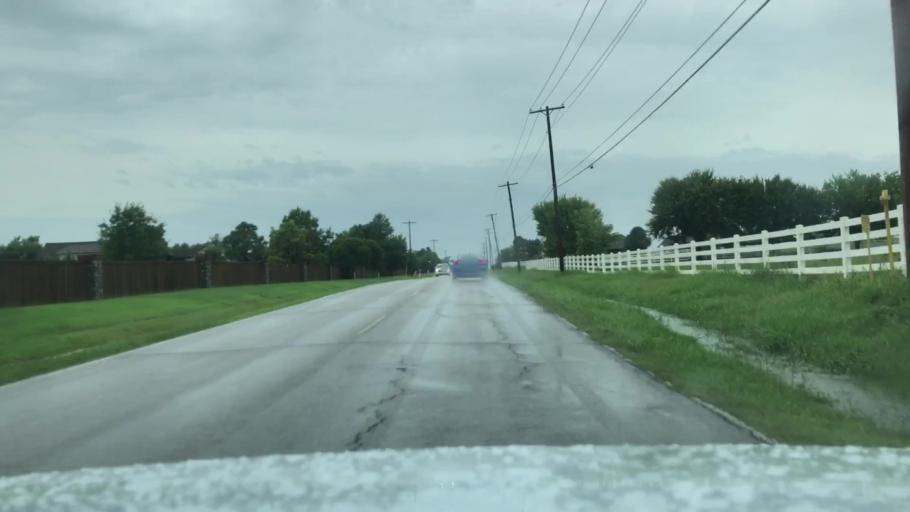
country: US
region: Oklahoma
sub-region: Tulsa County
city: Jenks
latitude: 36.0028
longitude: -95.9983
